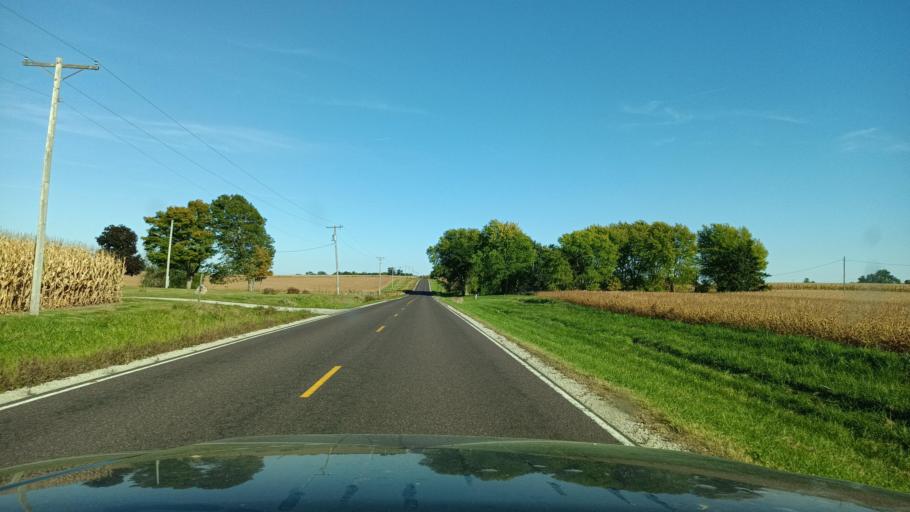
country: US
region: Illinois
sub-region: Logan County
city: Atlanta
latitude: 40.2386
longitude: -89.0981
